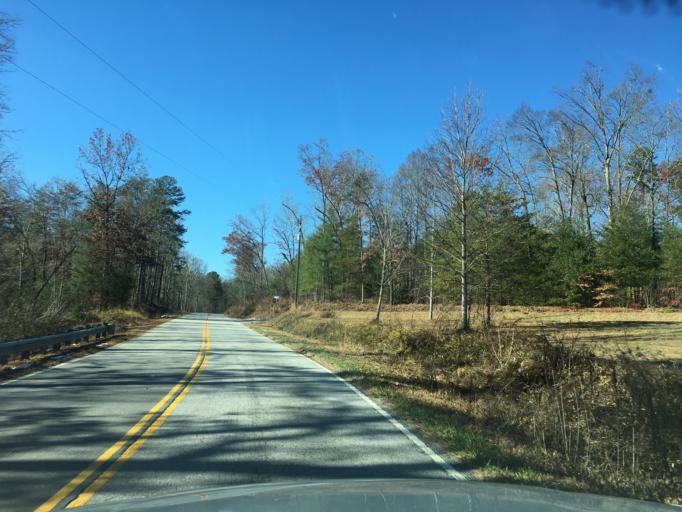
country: US
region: South Carolina
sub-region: Oconee County
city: Walhalla
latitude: 34.9330
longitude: -82.9904
